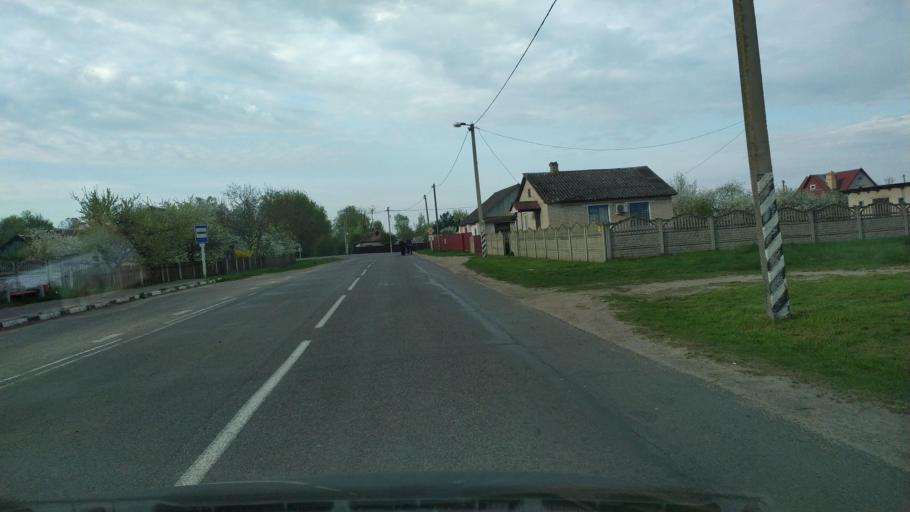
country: BY
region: Brest
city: Zhabinka
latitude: 52.1582
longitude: 24.0848
